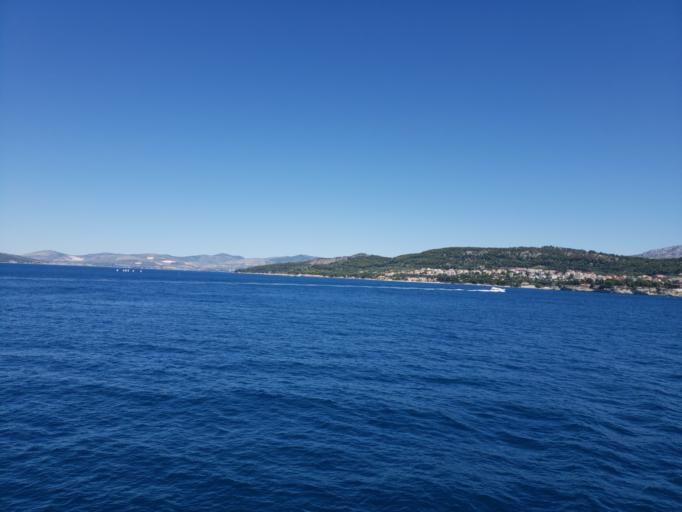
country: HR
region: Splitsko-Dalmatinska
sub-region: Grad Split
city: Split
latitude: 43.4891
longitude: 16.4323
